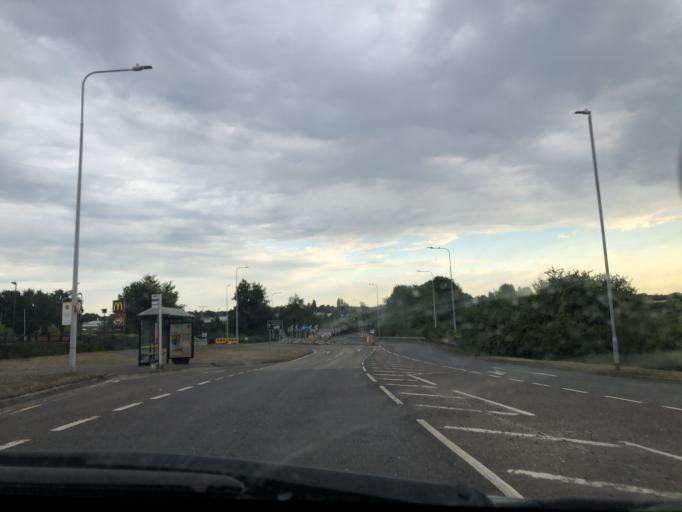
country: GB
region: England
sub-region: Kent
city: Sevenoaks
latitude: 51.2990
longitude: 0.1923
